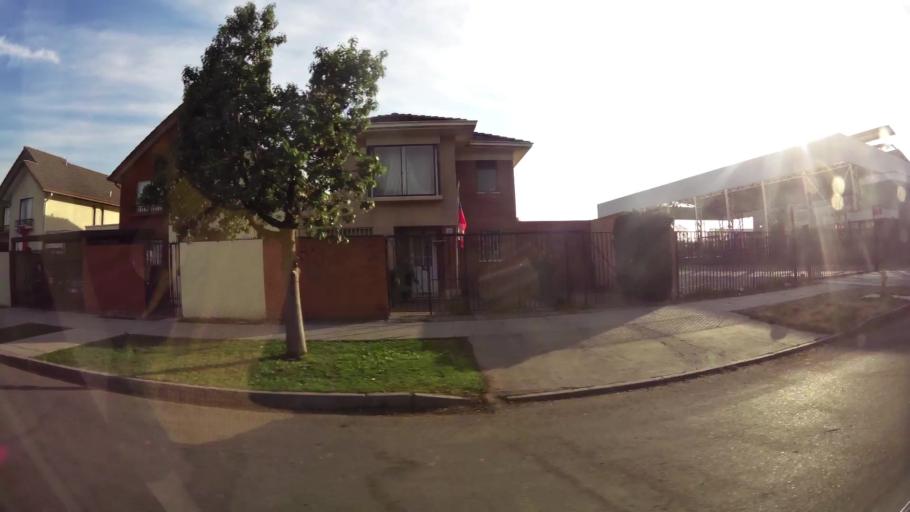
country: CL
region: Santiago Metropolitan
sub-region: Provincia de Maipo
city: San Bernardo
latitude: -33.5625
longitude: -70.7752
